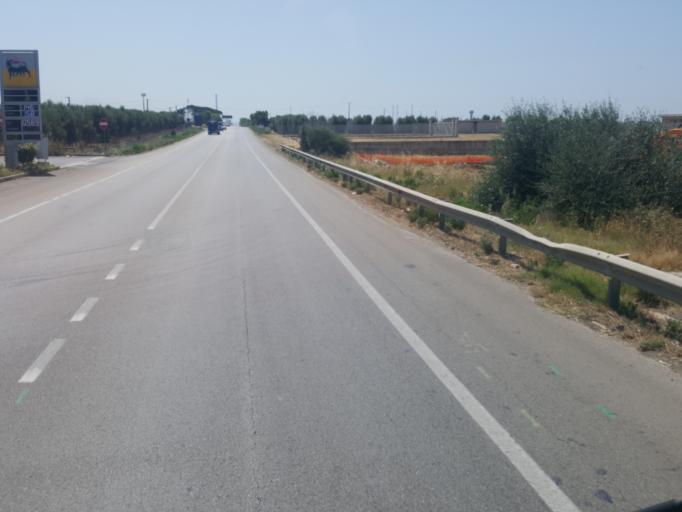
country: IT
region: Apulia
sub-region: Provincia di Taranto
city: Statte
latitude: 40.5301
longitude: 17.1675
